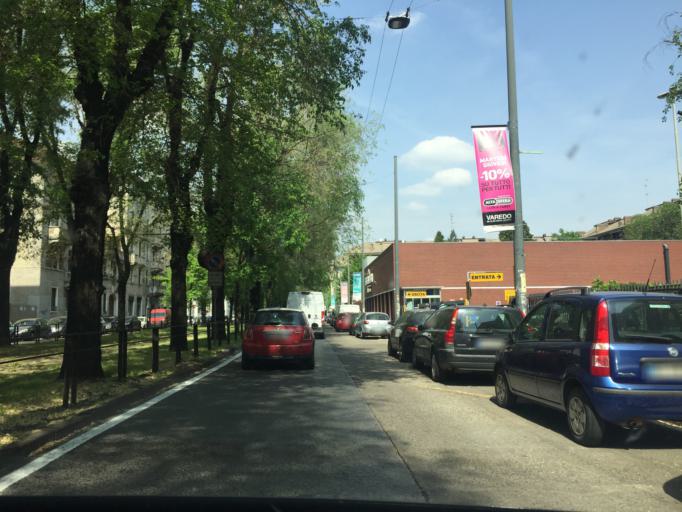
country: IT
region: Lombardy
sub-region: Citta metropolitana di Milano
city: Novate Milanese
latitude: 45.4969
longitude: 9.1542
